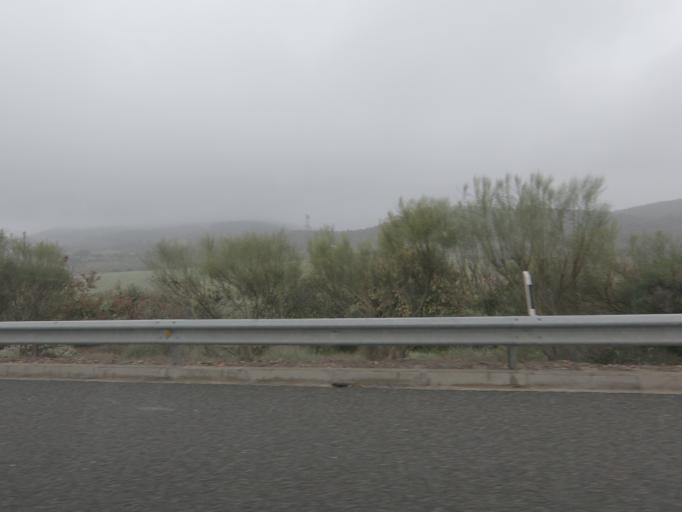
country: ES
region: Extremadura
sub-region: Provincia de Caceres
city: Canaveral
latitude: 39.8106
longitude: -6.3633
